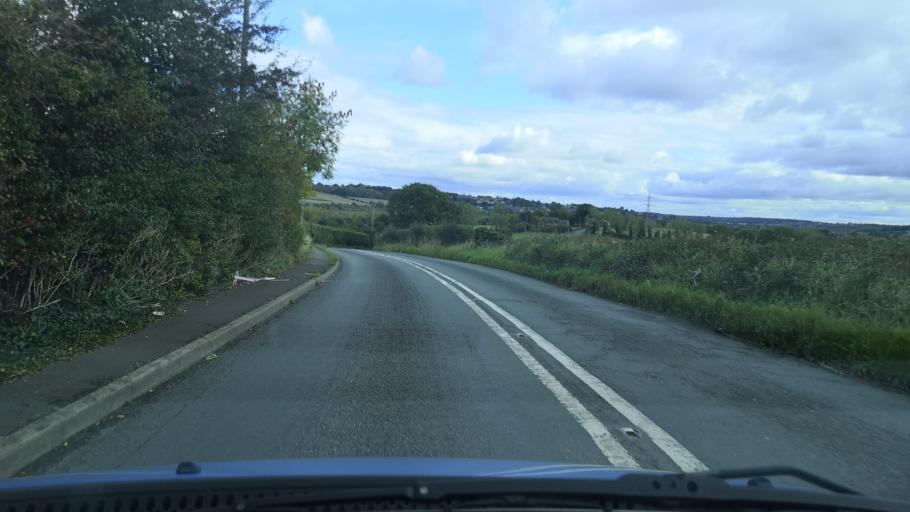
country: GB
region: England
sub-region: City and Borough of Wakefield
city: Middlestown
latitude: 53.6615
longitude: -1.6003
